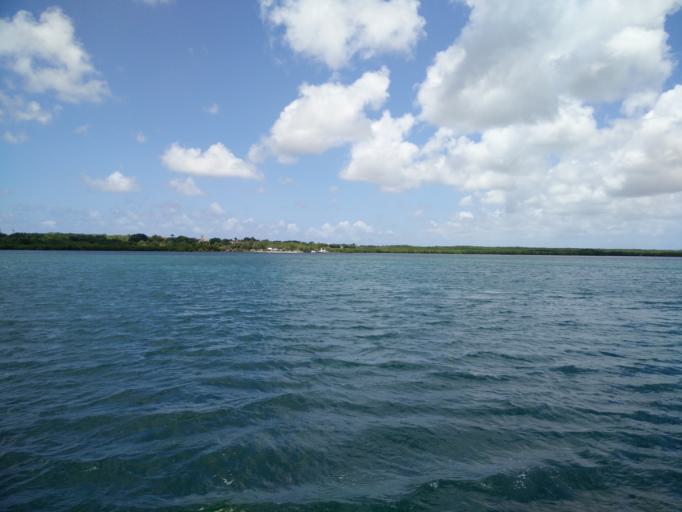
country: GP
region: Guadeloupe
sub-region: Guadeloupe
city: Petit-Canal
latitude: 16.3796
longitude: -61.5031
